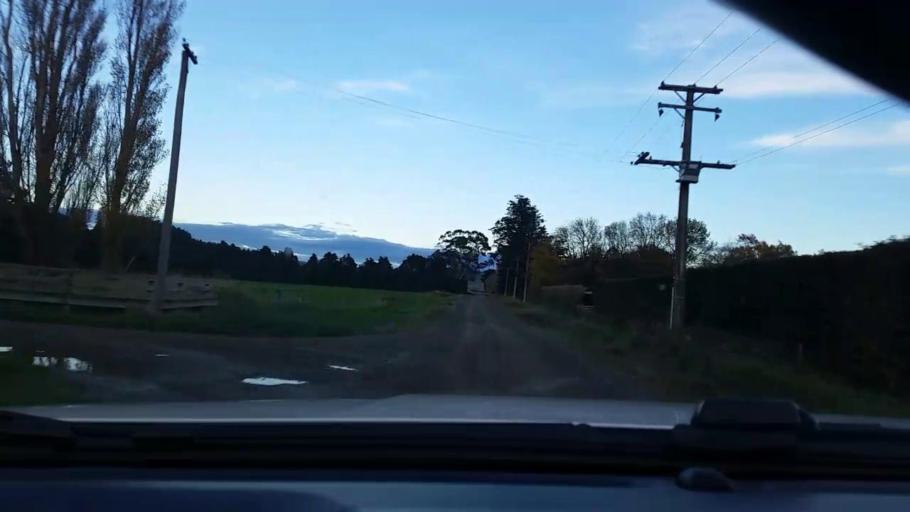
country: NZ
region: Southland
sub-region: Southland District
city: Winton
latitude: -46.1036
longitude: 168.4611
